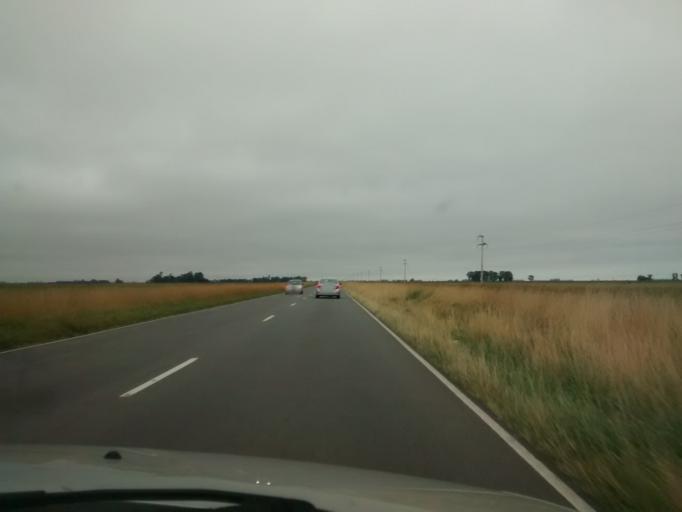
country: AR
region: Buenos Aires
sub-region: Partido de Ayacucho
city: Ayacucho
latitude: -37.0337
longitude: -58.5401
